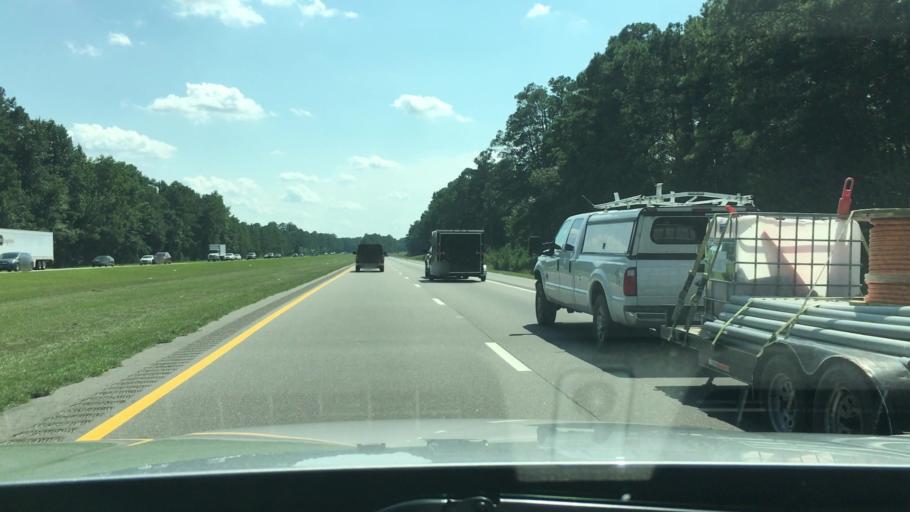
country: US
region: North Carolina
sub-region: Cumberland County
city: Hope Mills
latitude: 34.9530
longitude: -78.9001
